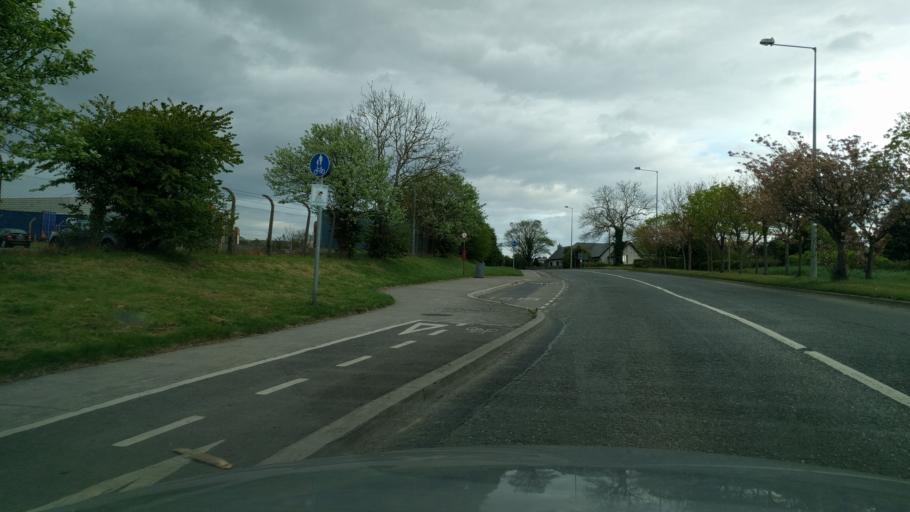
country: IE
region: Leinster
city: Balbriggan
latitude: 53.6007
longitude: -6.1854
